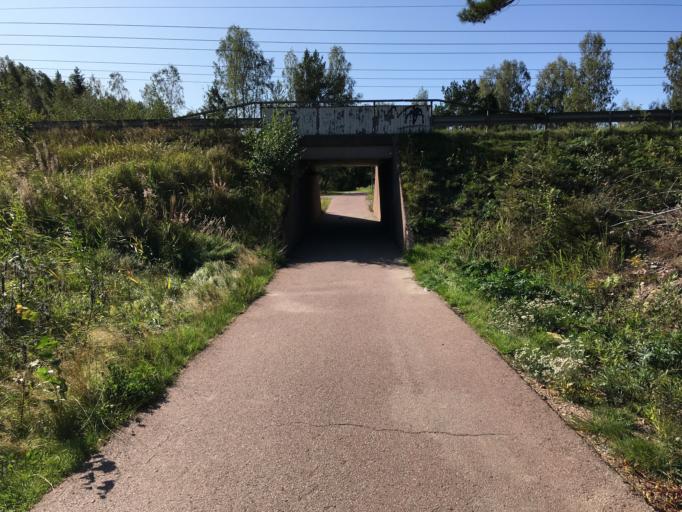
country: SE
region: Vaermland
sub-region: Karlstads Kommun
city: Karlstad
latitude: 59.3323
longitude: 13.5158
